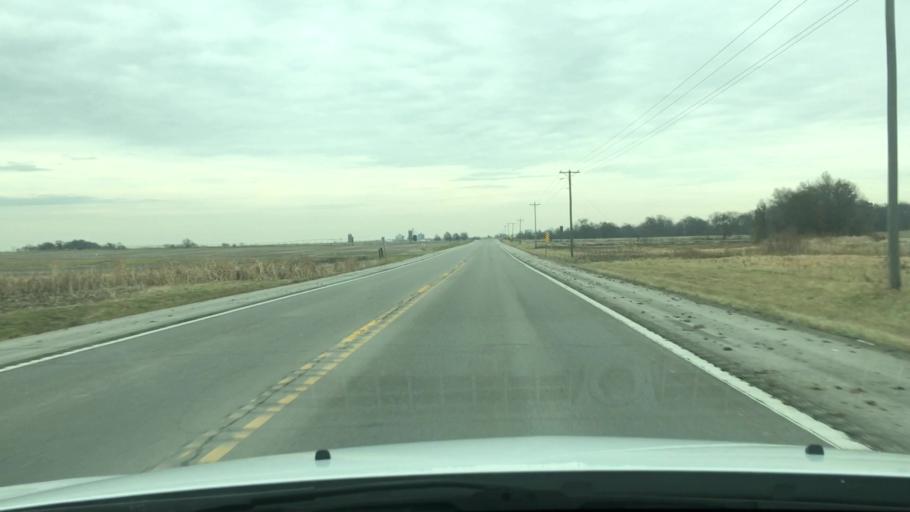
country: US
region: Missouri
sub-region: Audrain County
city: Mexico
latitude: 39.1642
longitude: -91.7187
